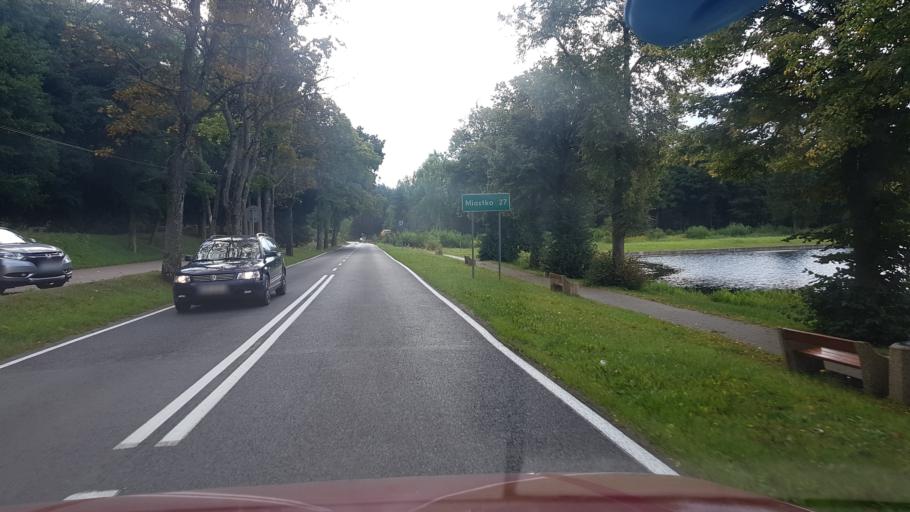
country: PL
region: West Pomeranian Voivodeship
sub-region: Powiat koszalinski
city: Polanow
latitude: 54.1192
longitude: 16.6947
